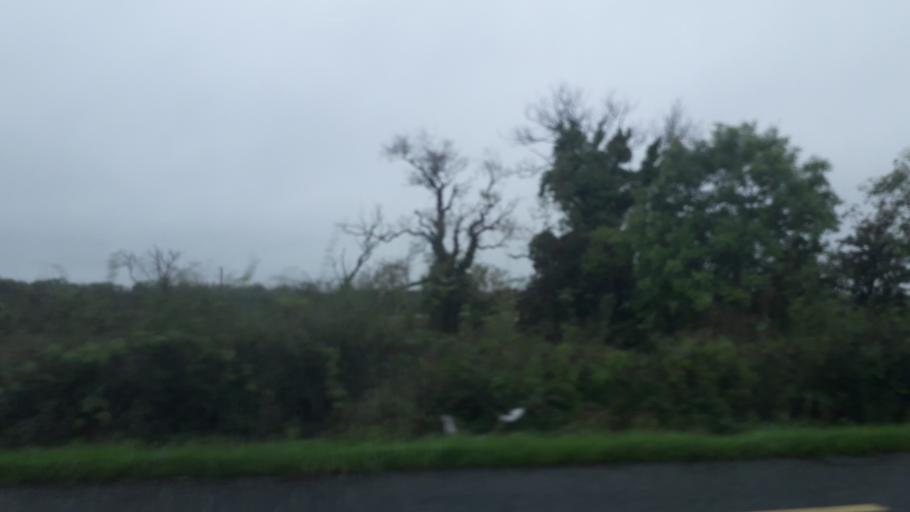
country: IE
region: Leinster
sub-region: An Longfort
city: Edgeworthstown
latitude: 53.7012
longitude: -7.6418
